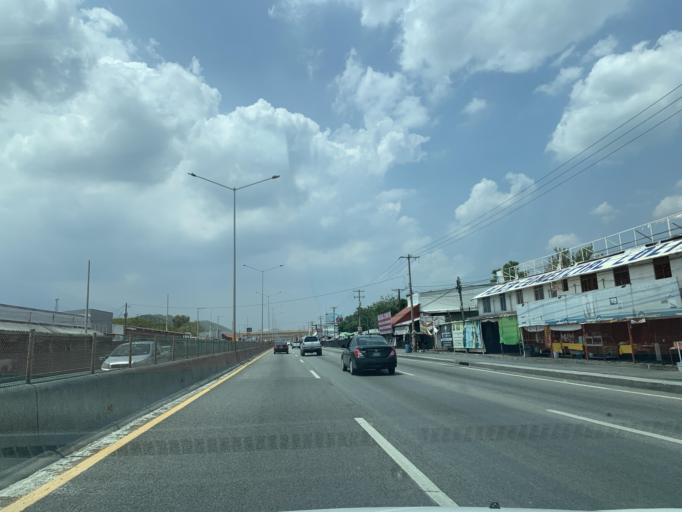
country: MX
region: Nuevo Leon
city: Santiago
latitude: 25.4482
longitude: -100.1600
